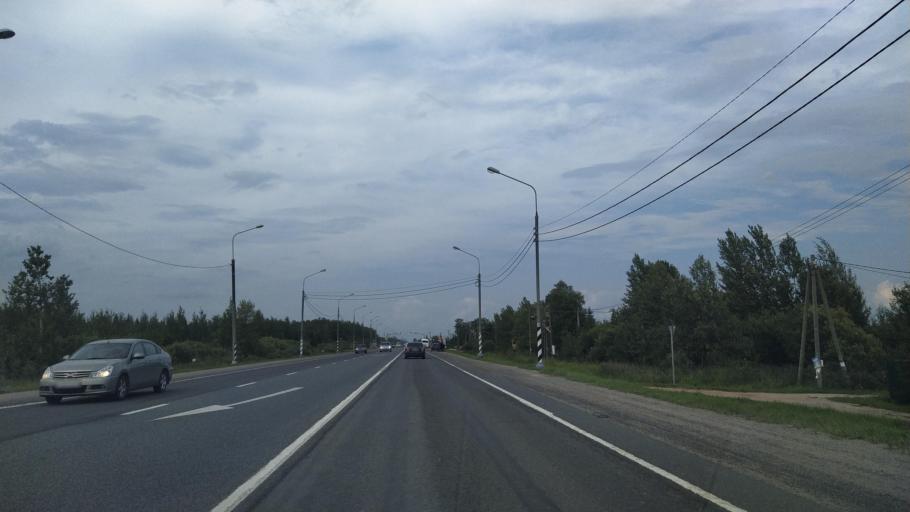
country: RU
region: Novgorod
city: Pankovka
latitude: 58.4761
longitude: 31.1773
